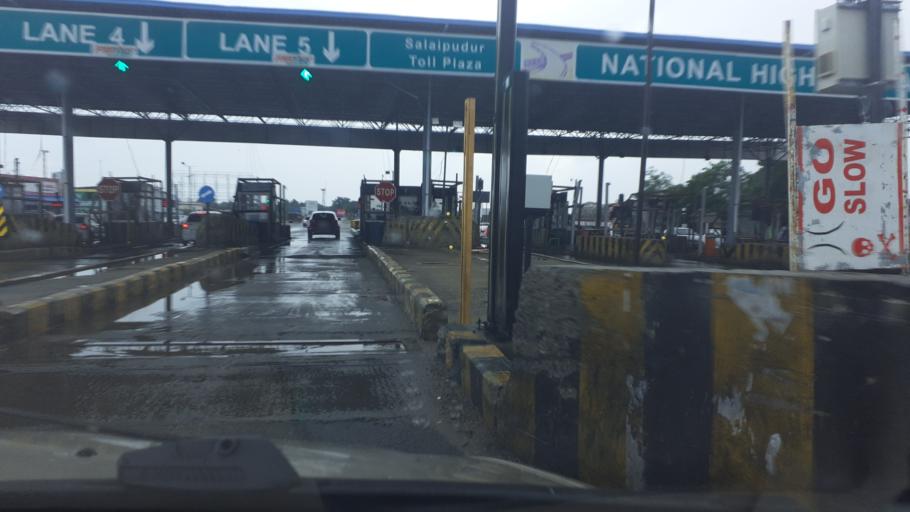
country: IN
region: Tamil Nadu
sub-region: Thoothukkudi
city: Kayattar
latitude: 8.9761
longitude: 77.7747
